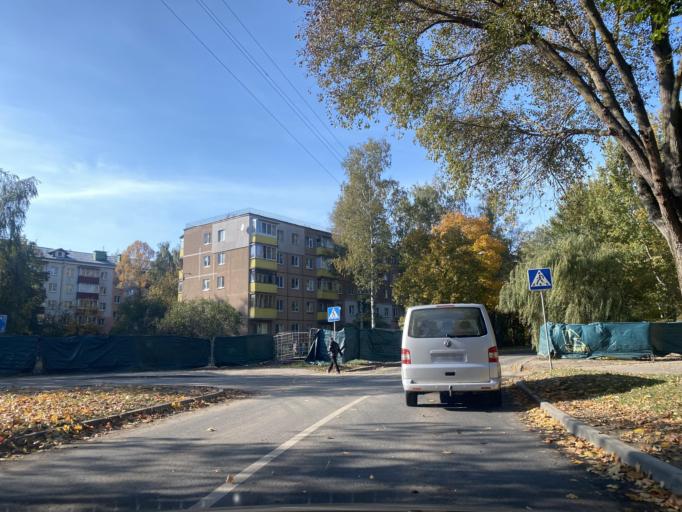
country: BY
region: Minsk
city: Borovlyany
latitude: 53.9503
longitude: 27.6303
